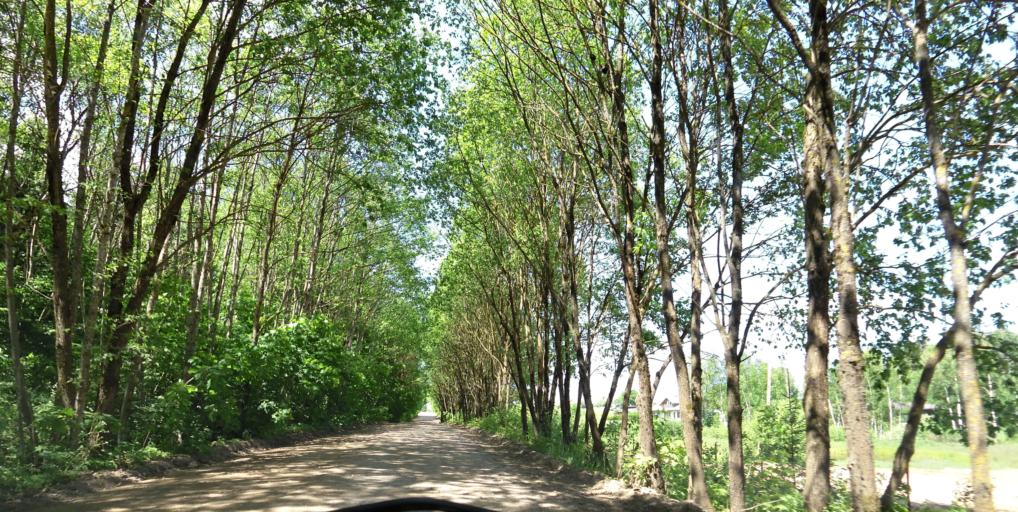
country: LT
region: Vilnius County
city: Pilaite
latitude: 54.7434
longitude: 25.1368
